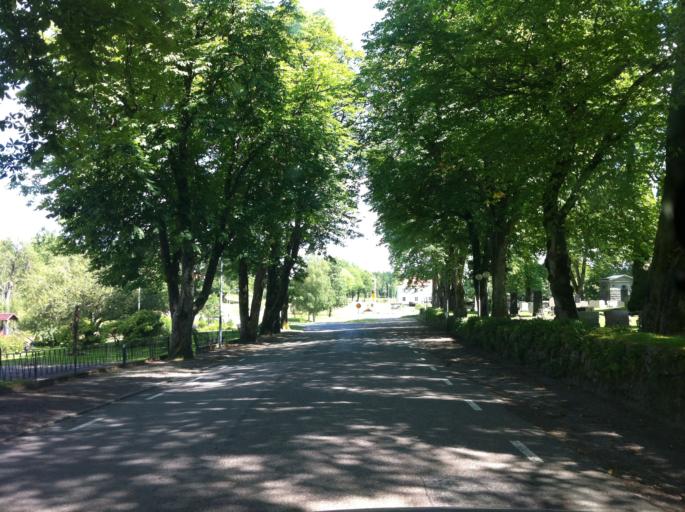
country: SE
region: Joenkoeping
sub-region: Gislaveds Kommun
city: Gislaved
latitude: 57.3468
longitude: 13.5241
